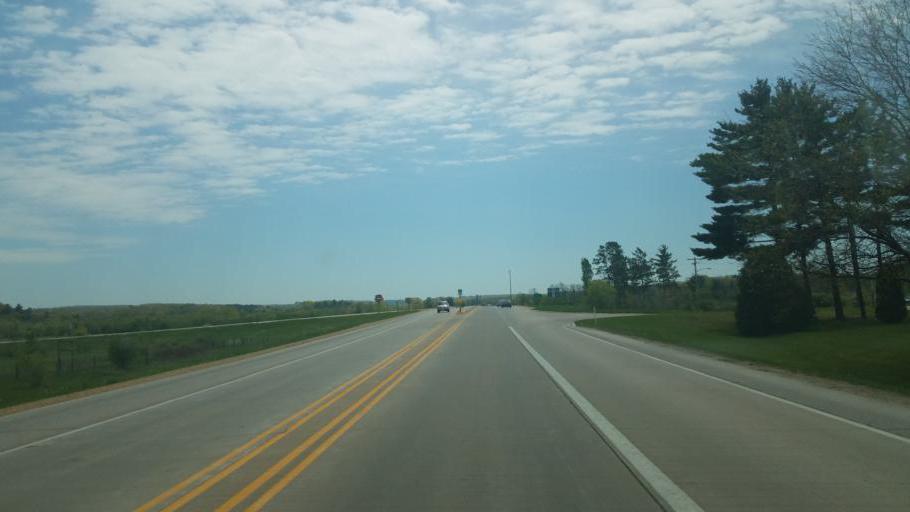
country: US
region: Wisconsin
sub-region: Monroe County
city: Tomah
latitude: 43.9603
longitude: -90.5048
